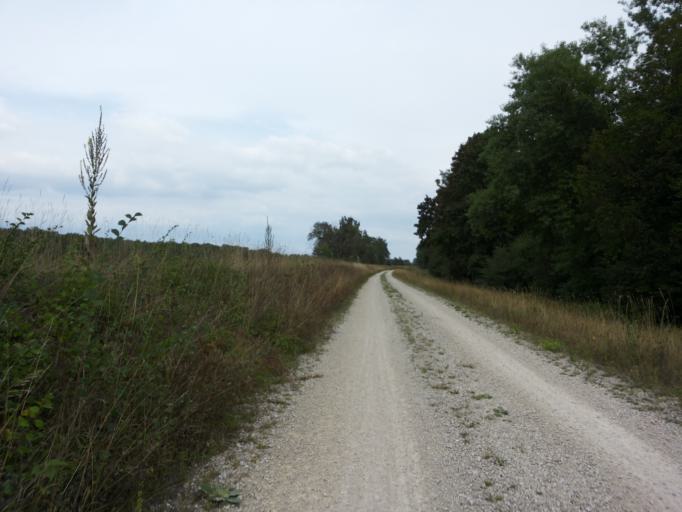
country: DE
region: Bavaria
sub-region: Upper Bavaria
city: Bergheim
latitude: 48.7487
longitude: 11.2445
